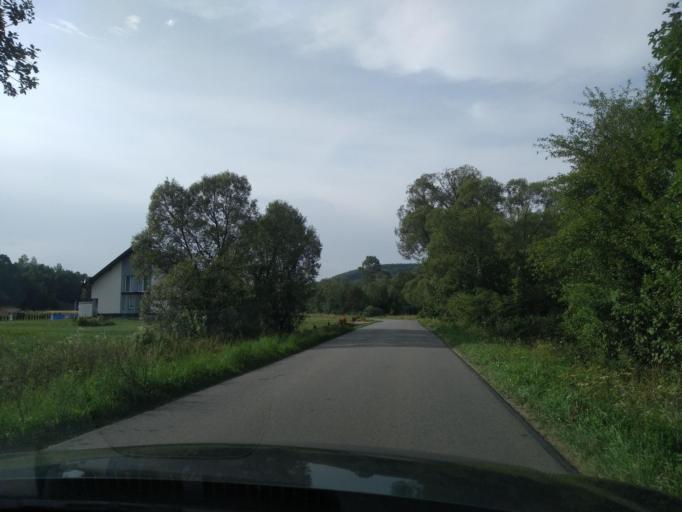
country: PL
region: Subcarpathian Voivodeship
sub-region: Powiat sanocki
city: Tyrawa Woloska
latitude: 49.5647
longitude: 22.3871
